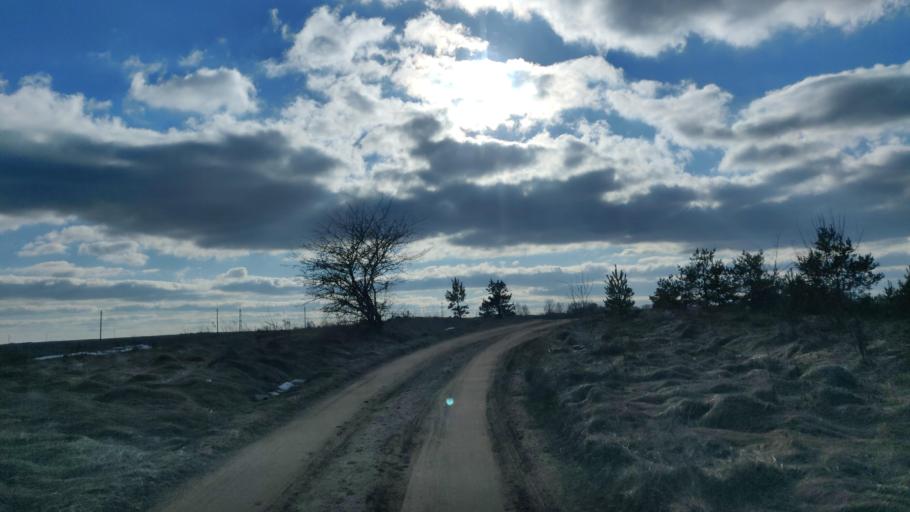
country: LT
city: Lentvaris
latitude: 54.6103
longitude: 24.9985
